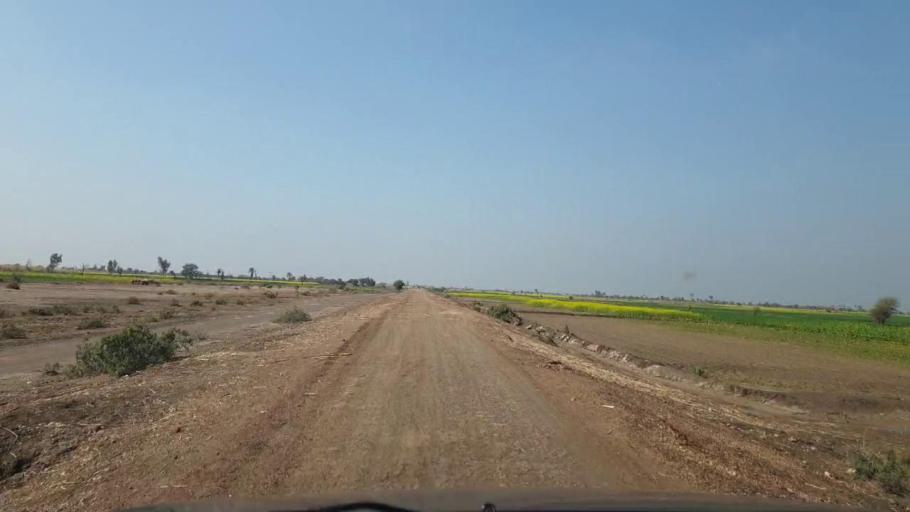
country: PK
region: Sindh
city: Sinjhoro
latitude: 26.0461
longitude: 68.7555
